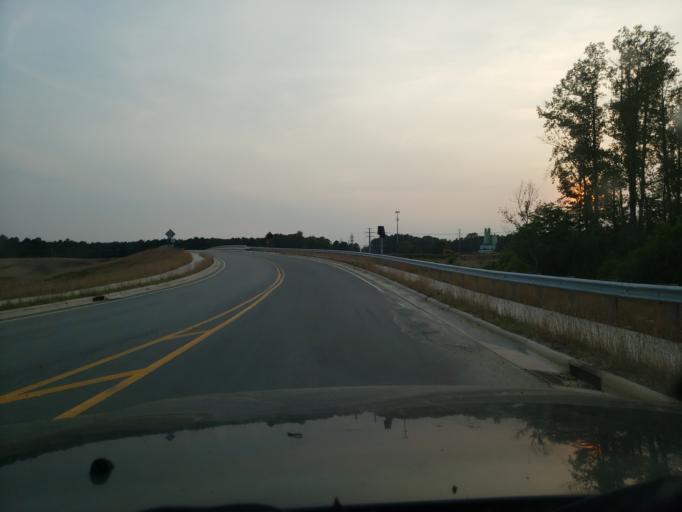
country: US
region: North Carolina
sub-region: Durham County
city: Durham
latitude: 35.9815
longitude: -78.8554
